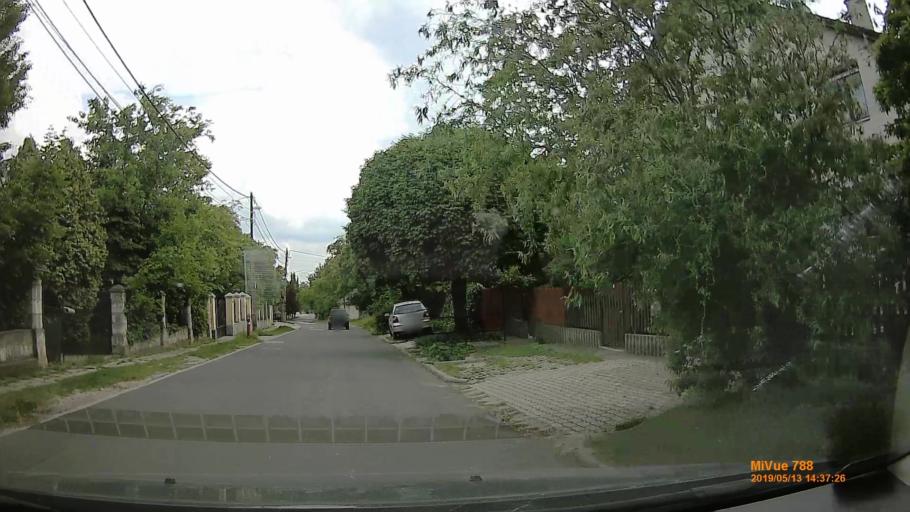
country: HU
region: Budapest
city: Budapest XXII. keruelet
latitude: 47.4211
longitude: 19.0108
